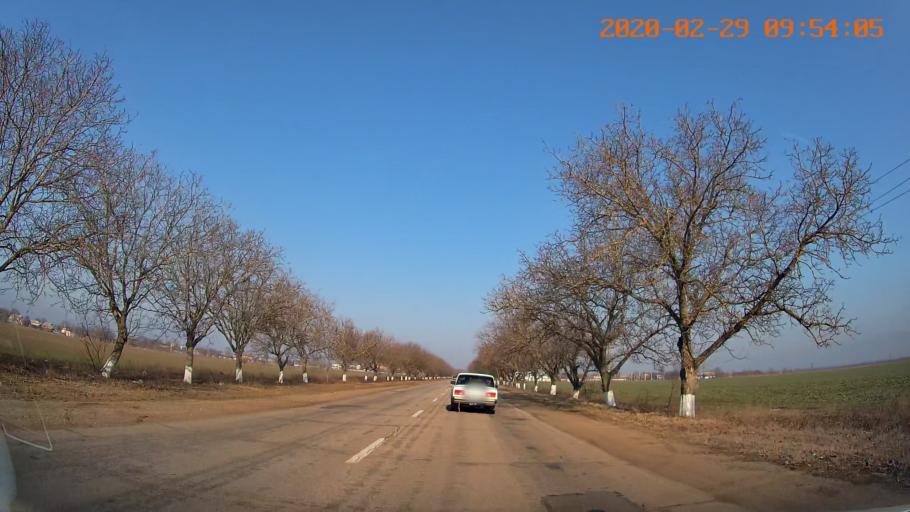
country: MD
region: Telenesti
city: Slobozia
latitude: 46.7262
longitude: 29.7180
